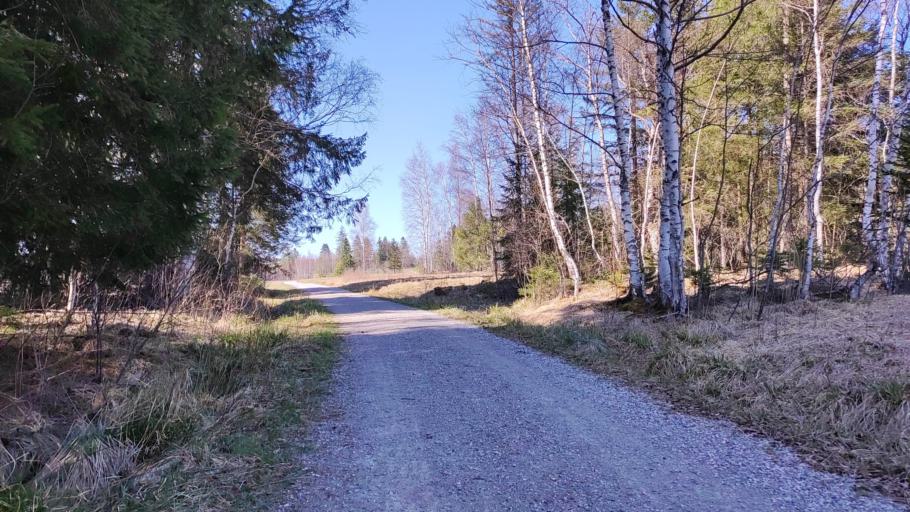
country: DE
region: Bavaria
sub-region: Upper Bavaria
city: Unterammergau
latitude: 47.6359
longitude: 11.0262
